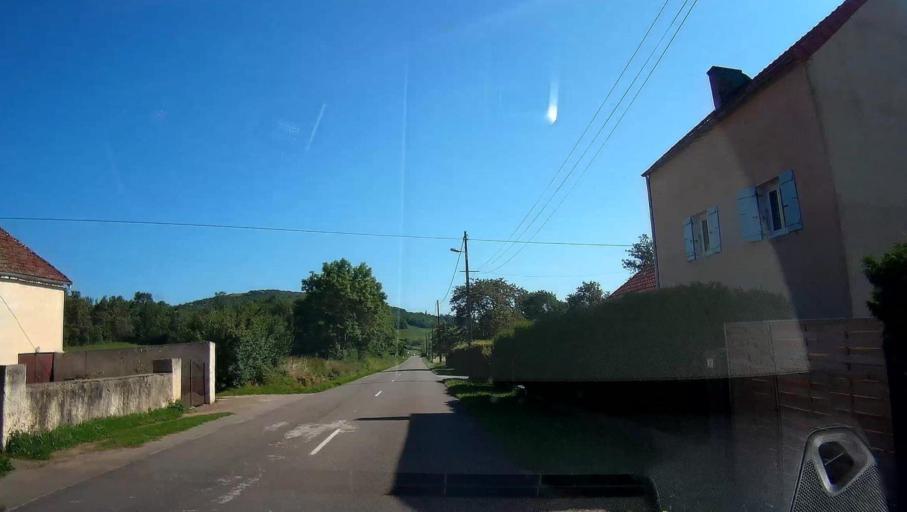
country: FR
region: Bourgogne
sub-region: Departement de la Cote-d'Or
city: Nolay
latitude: 46.9155
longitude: 4.6018
